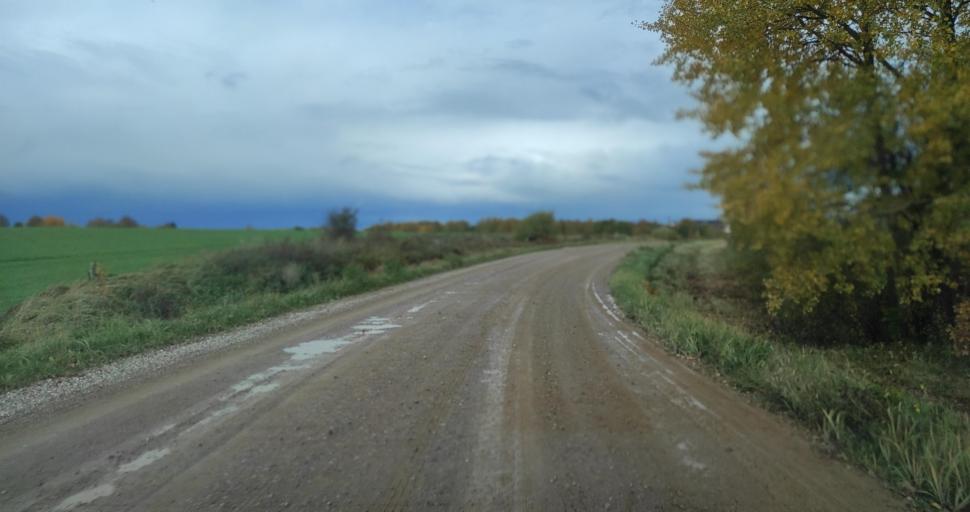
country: LV
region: Vainode
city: Vainode
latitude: 56.5585
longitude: 21.9072
